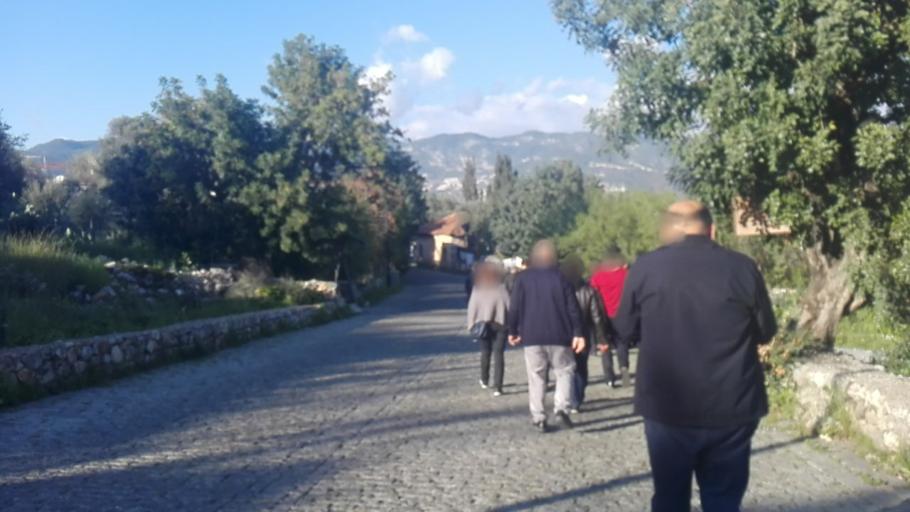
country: TR
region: Antalya
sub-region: Alanya
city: Alanya
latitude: 36.5322
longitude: 31.9931
